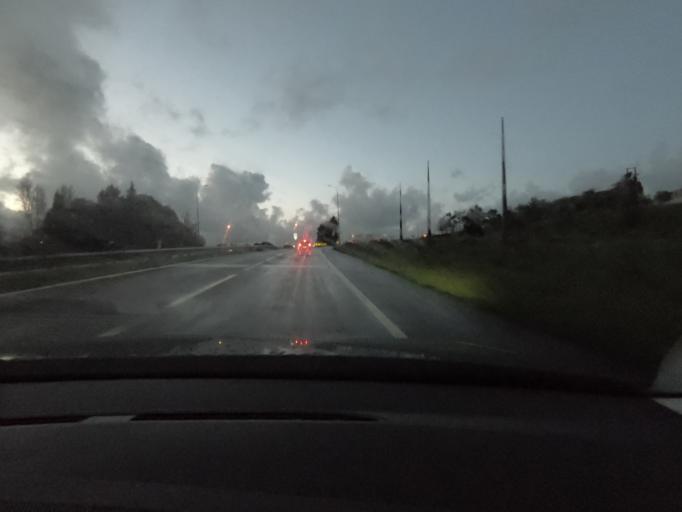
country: PT
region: Lisbon
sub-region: Sintra
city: Cacem
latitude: 38.7459
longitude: -9.3031
